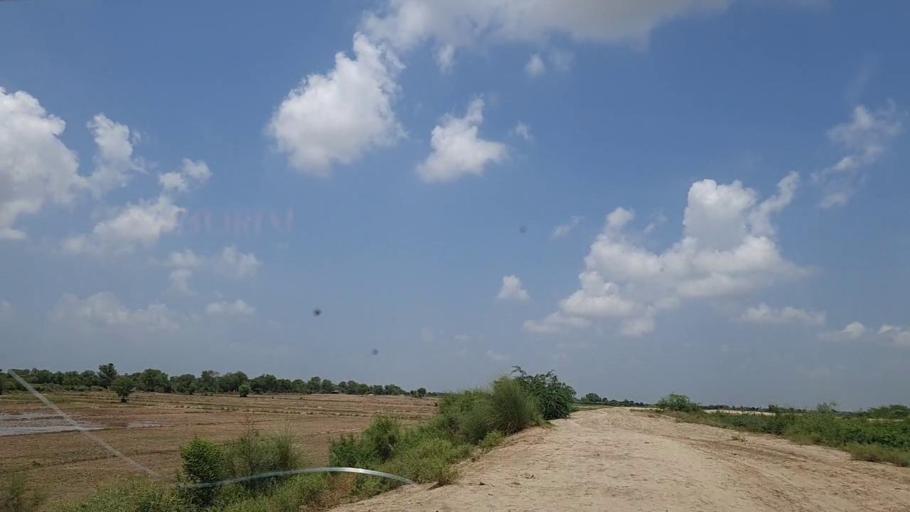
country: PK
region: Sindh
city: Tharu Shah
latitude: 26.9455
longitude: 68.0143
